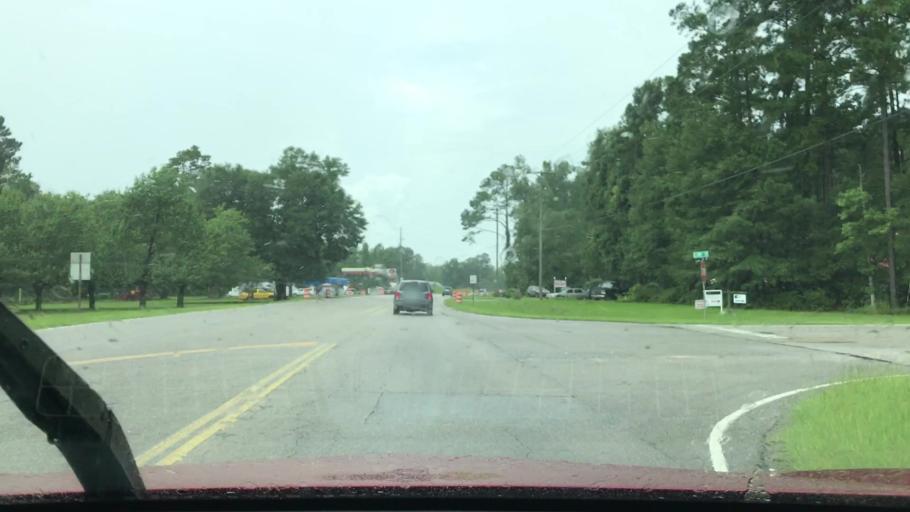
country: US
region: South Carolina
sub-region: Horry County
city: Red Hill
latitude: 33.8770
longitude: -78.9722
